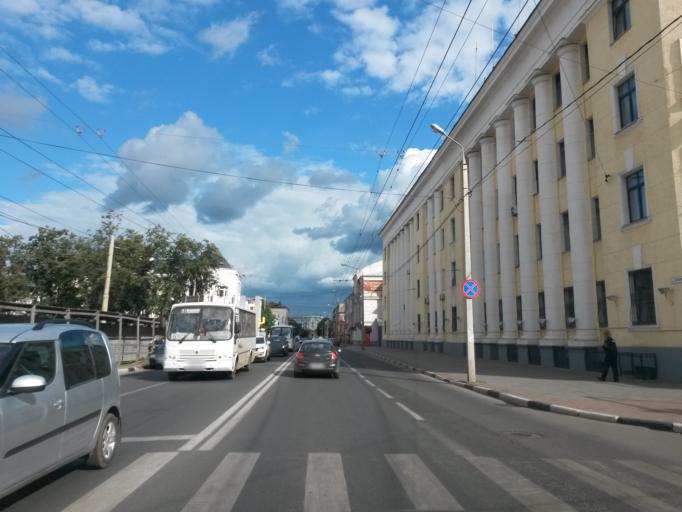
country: RU
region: Jaroslavl
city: Yaroslavl
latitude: 57.6331
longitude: 39.8805
